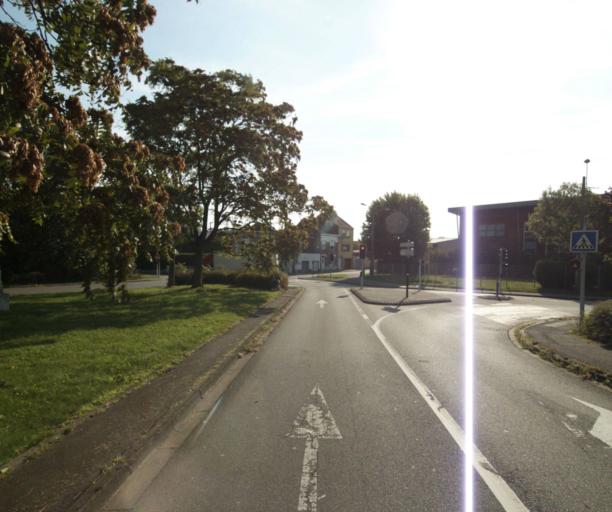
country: FR
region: Nord-Pas-de-Calais
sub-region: Departement du Nord
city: Lomme
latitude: 50.6489
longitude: 2.9850
